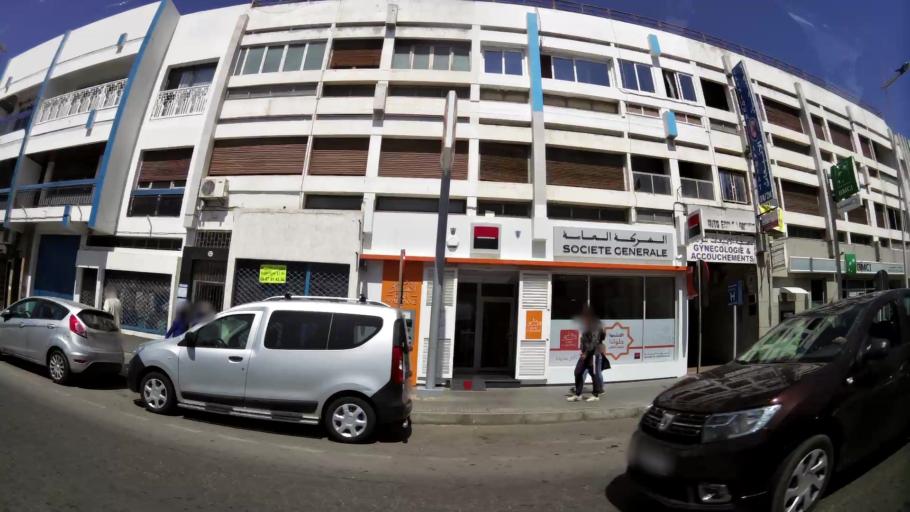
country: MA
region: Souss-Massa-Draa
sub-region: Agadir-Ida-ou-Tnan
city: Agadir
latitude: 30.4132
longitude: -9.5924
